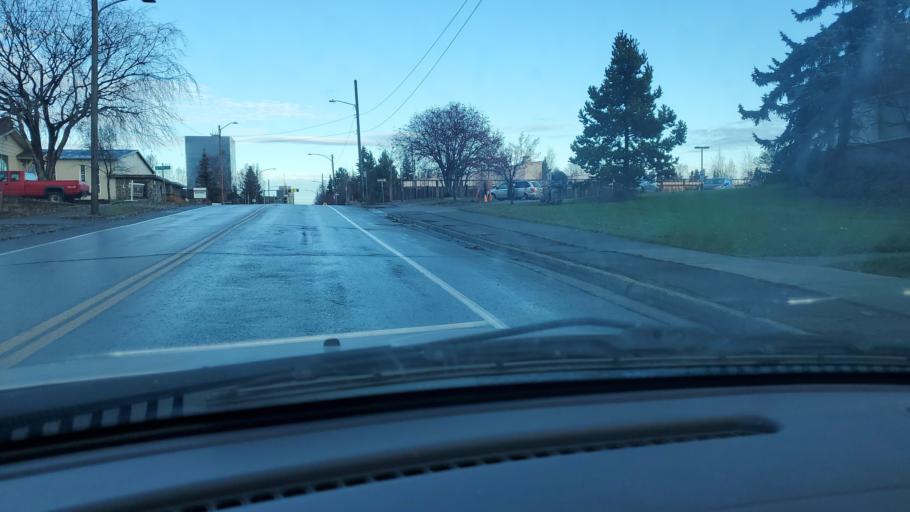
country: US
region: Alaska
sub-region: Anchorage Municipality
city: Anchorage
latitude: 61.2091
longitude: -149.8914
